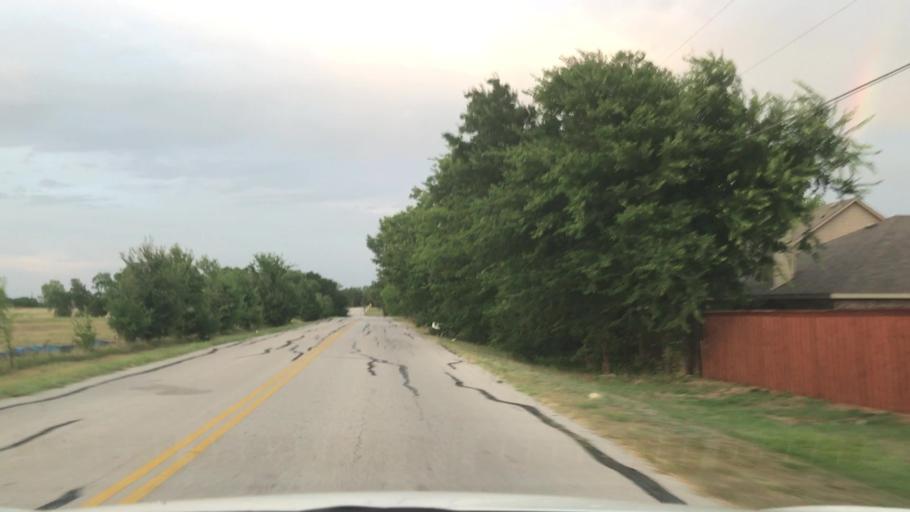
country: US
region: Texas
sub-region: Dallas County
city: Seagoville
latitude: 32.6936
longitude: -96.5532
